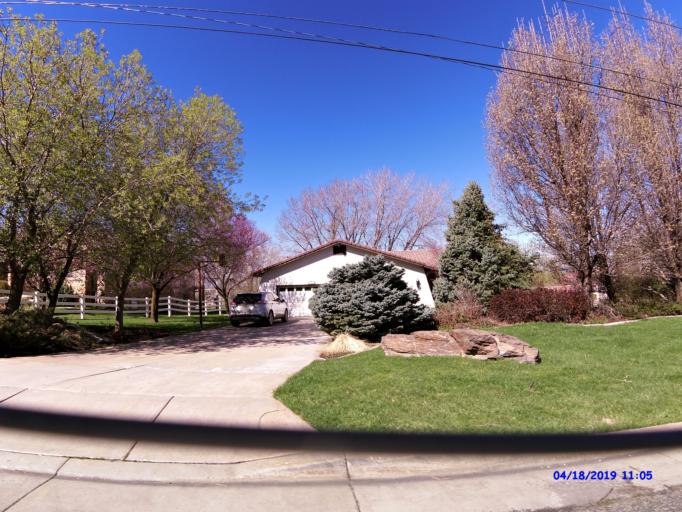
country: US
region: Utah
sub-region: Weber County
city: North Ogden
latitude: 41.2884
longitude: -111.9481
